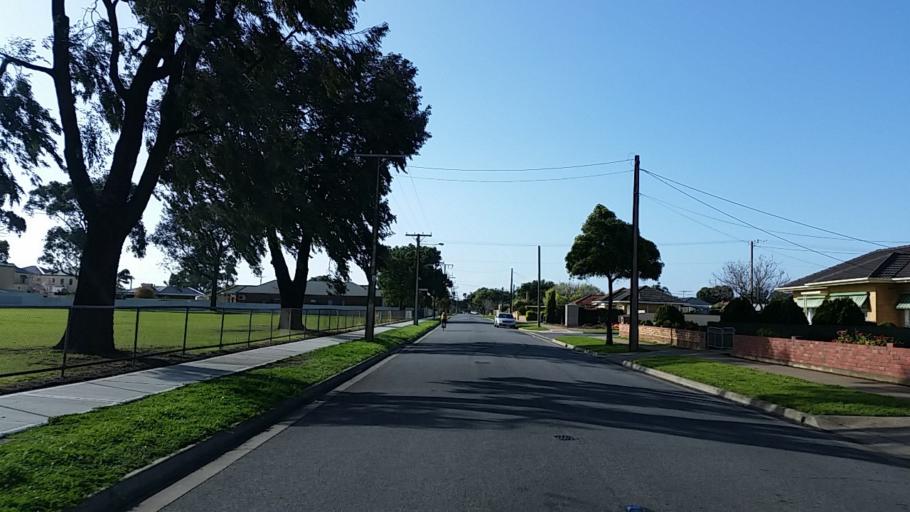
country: AU
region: South Australia
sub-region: Charles Sturt
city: Findon
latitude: -34.8982
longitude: 138.5276
